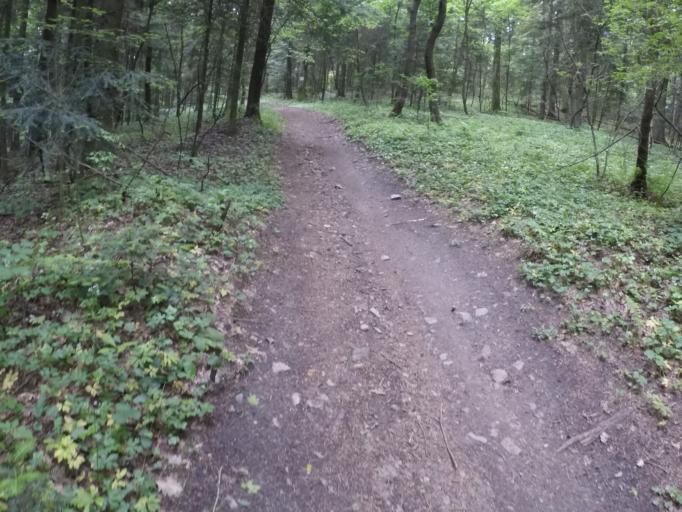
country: PL
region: Swietokrzyskie
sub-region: Powiat kielecki
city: Kielce
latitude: 50.8382
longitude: 20.6000
